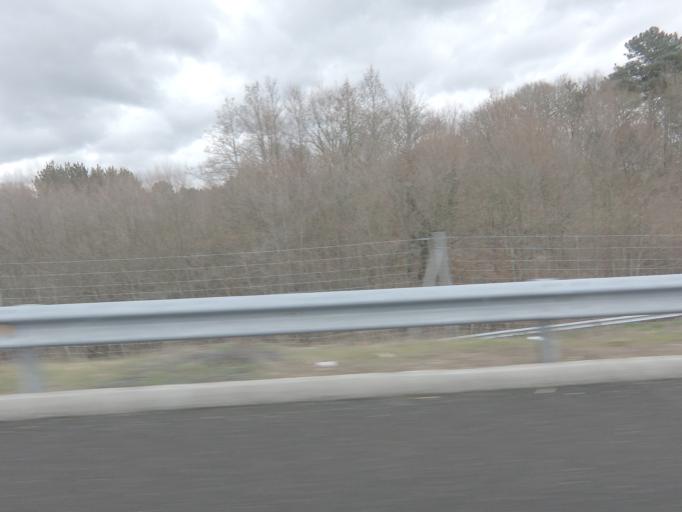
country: ES
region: Galicia
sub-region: Provincia de Ourense
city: Maside
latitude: 42.4344
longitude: -8.0176
